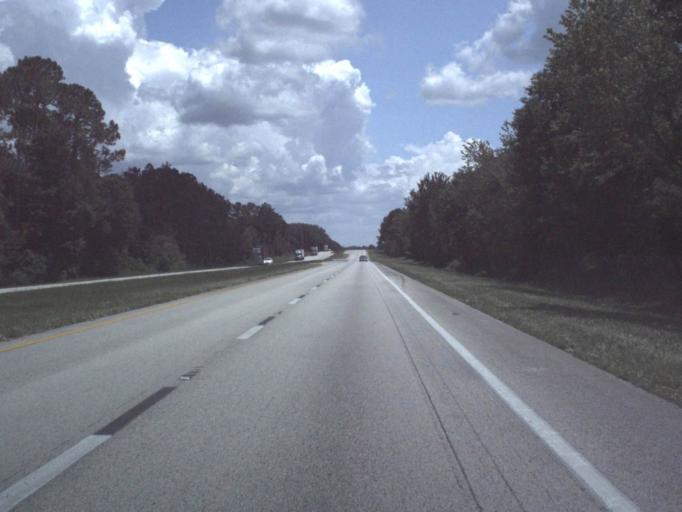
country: US
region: Florida
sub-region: Alachua County
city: Hawthorne
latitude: 29.6360
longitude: -82.1043
